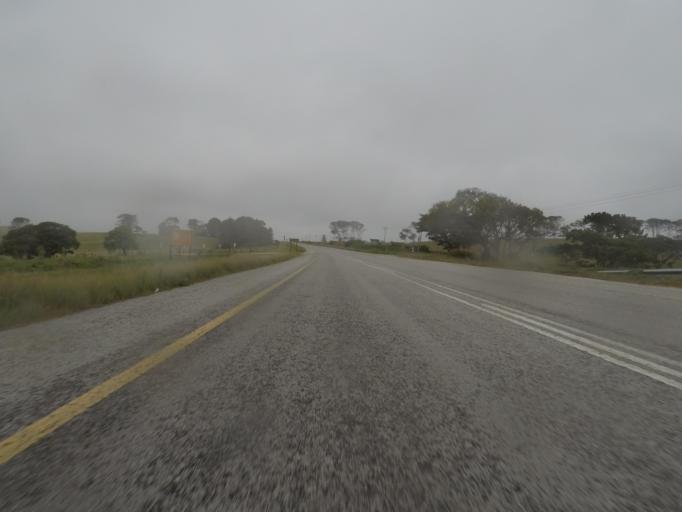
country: ZA
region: Eastern Cape
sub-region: Cacadu District Municipality
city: Grahamstown
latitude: -33.6440
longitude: 26.3542
